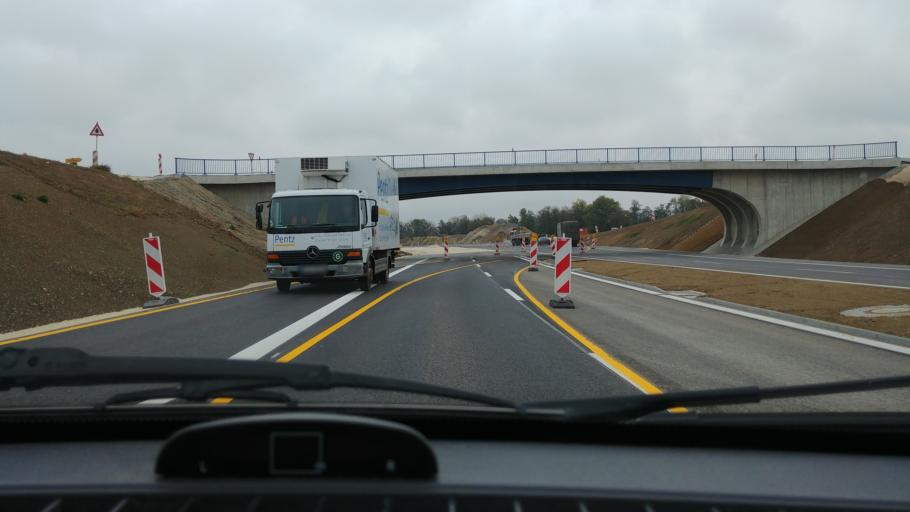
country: DE
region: Baden-Wuerttemberg
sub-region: Regierungsbezirk Stuttgart
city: Mogglingen
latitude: 48.8220
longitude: 9.9896
